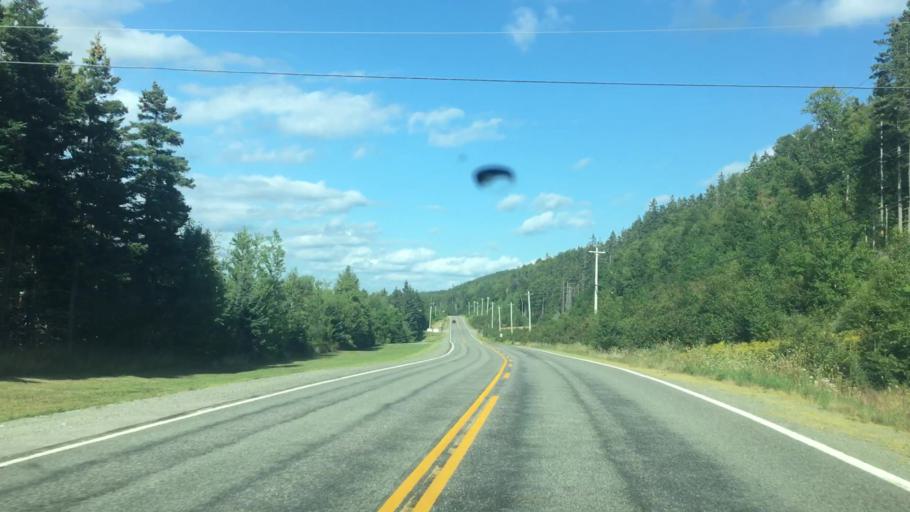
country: CA
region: Nova Scotia
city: Sydney
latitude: 45.8679
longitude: -60.6133
